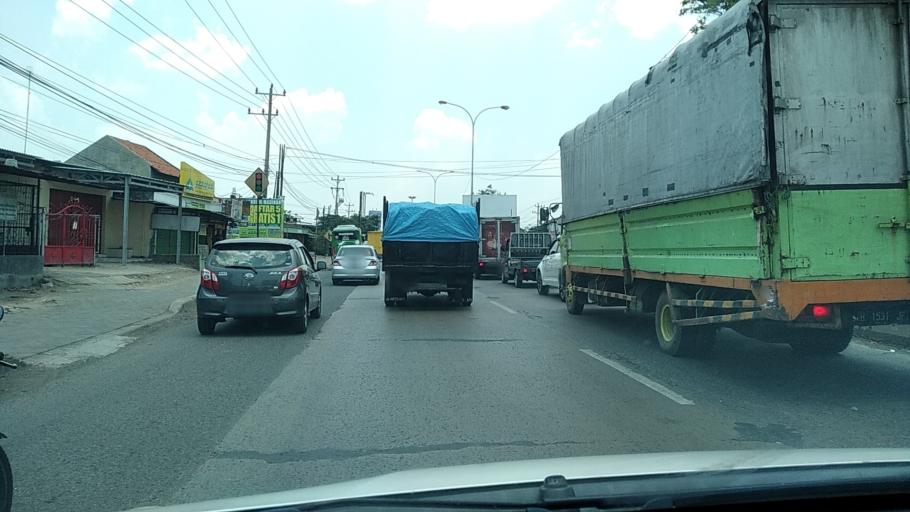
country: ID
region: Central Java
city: Semarang
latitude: -6.9518
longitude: 110.4795
